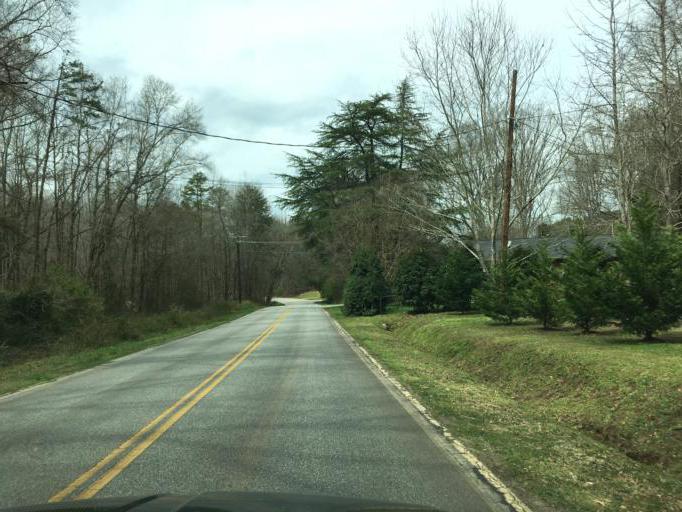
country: US
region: South Carolina
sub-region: Anderson County
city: Pendleton
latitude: 34.6576
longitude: -82.7790
